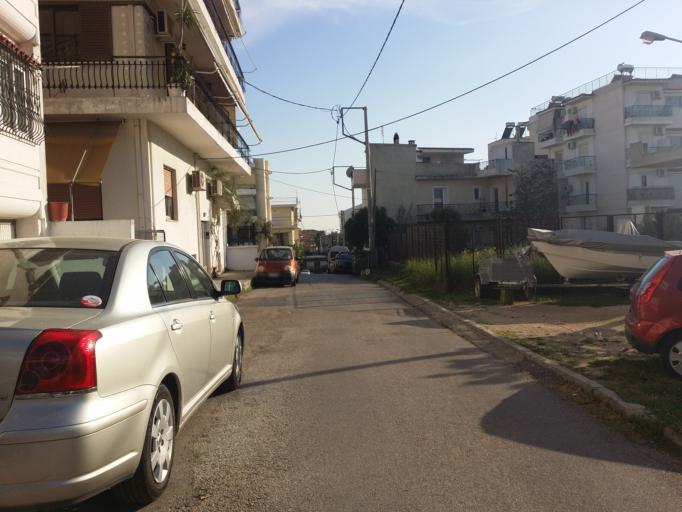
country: GR
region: Attica
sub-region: Nomarchia Athinas
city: Irakleio
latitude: 38.0541
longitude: 23.7544
